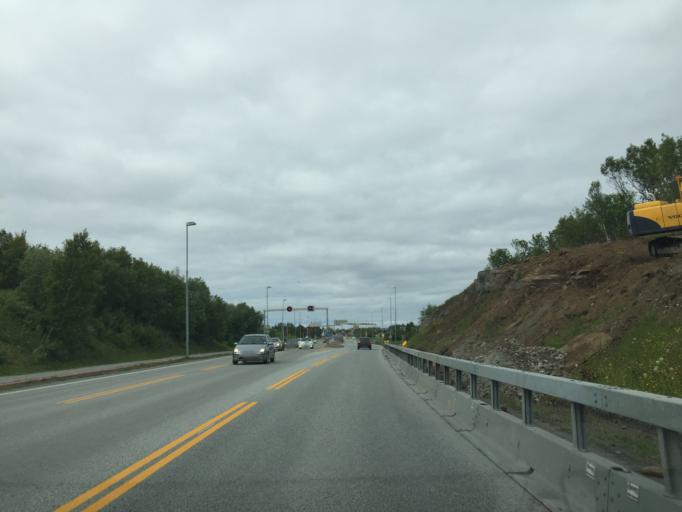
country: NO
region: Nordland
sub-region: Bodo
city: Bodo
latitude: 67.2771
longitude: 14.4367
